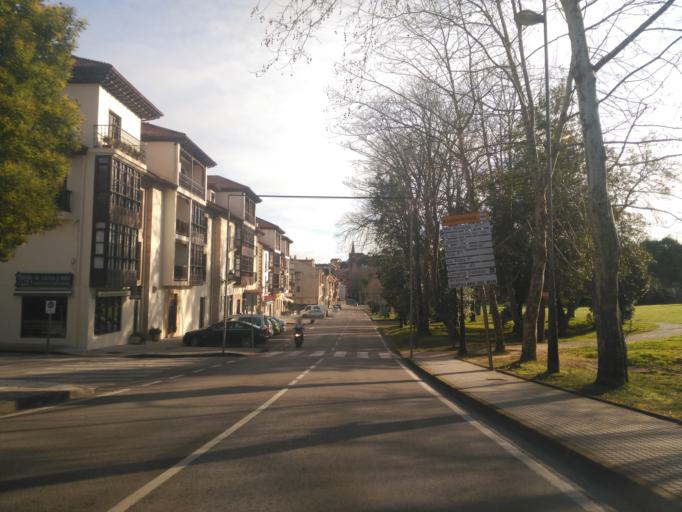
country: ES
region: Cantabria
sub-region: Provincia de Cantabria
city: Comillas
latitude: 43.3846
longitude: -4.2965
